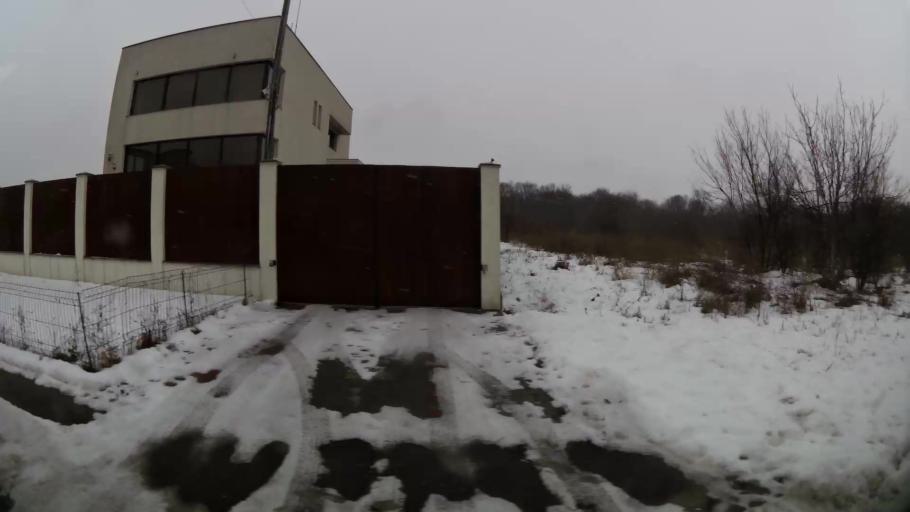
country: RO
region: Ilfov
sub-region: Comuna Mogosoaia
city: Mogosoaia
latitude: 44.5089
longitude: 26.0147
